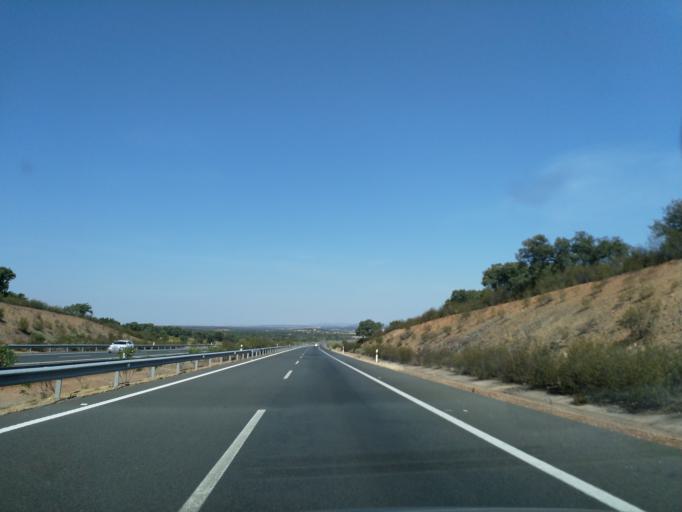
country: ES
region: Extremadura
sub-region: Provincia de Caceres
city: Alcuescar
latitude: 39.1782
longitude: -6.2728
